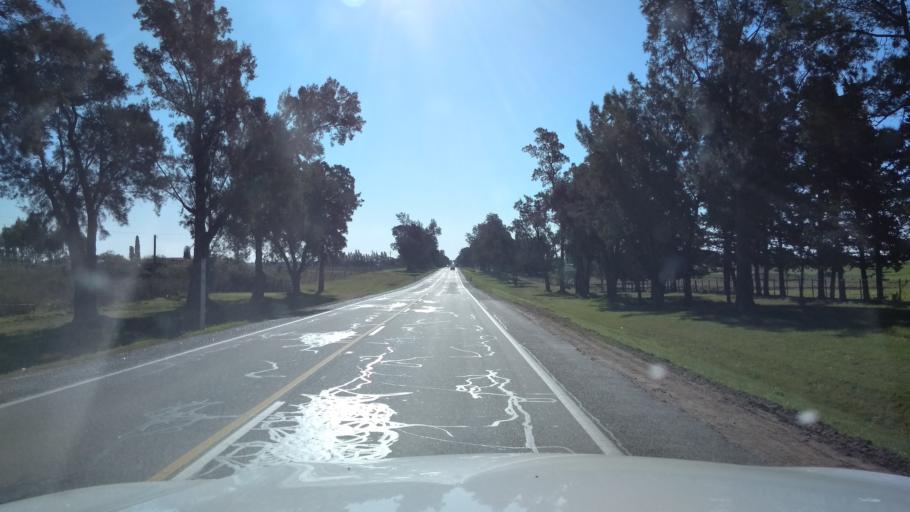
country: UY
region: Canelones
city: San Jacinto
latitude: -34.5888
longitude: -55.8375
